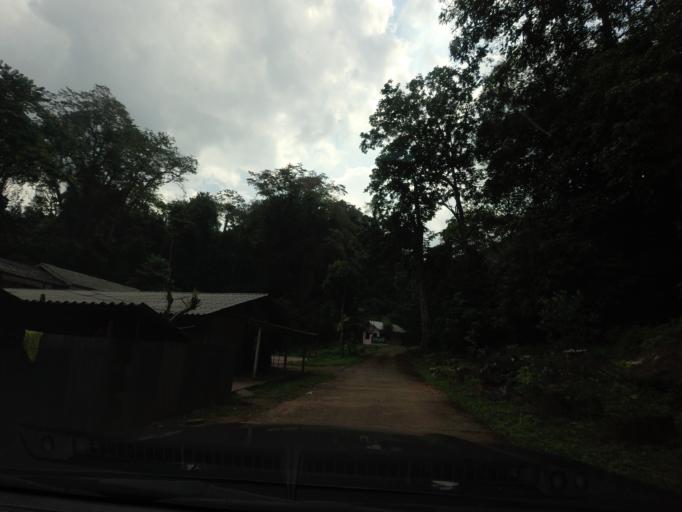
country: TH
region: Nan
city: Bo Kluea
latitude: 19.1911
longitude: 101.1990
